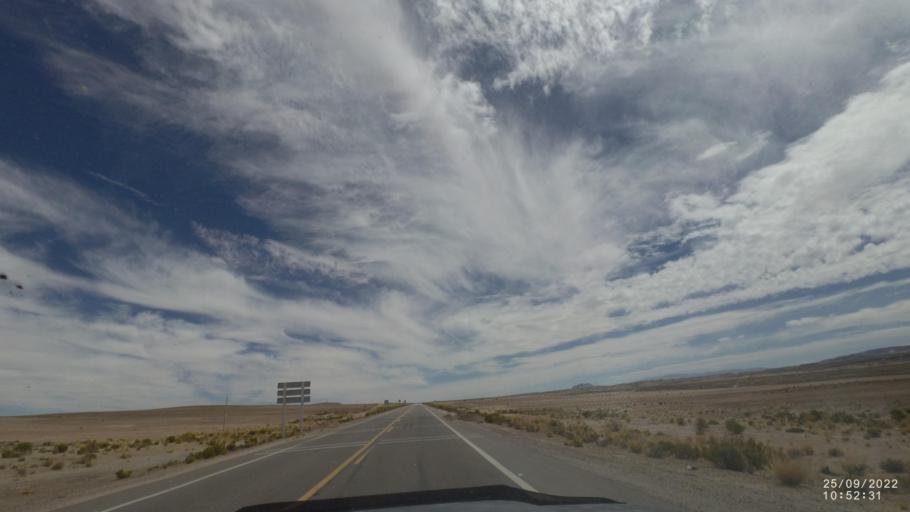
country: BO
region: Oruro
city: Challapata
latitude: -19.5472
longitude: -66.8535
